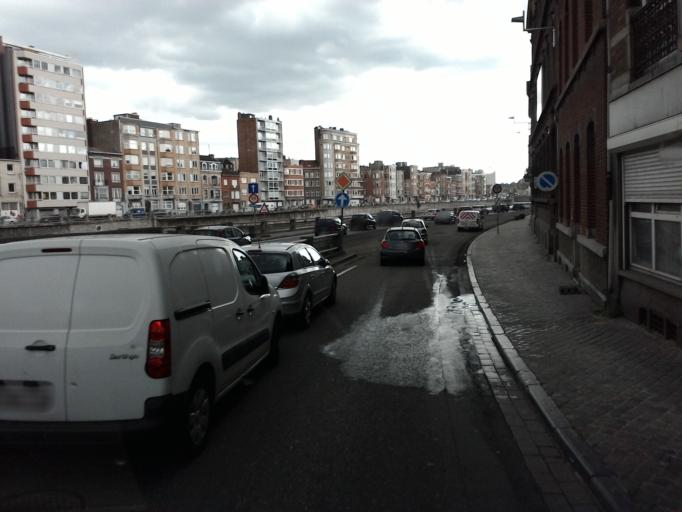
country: BE
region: Wallonia
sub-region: Province de Liege
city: Liege
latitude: 50.6367
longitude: 5.5802
